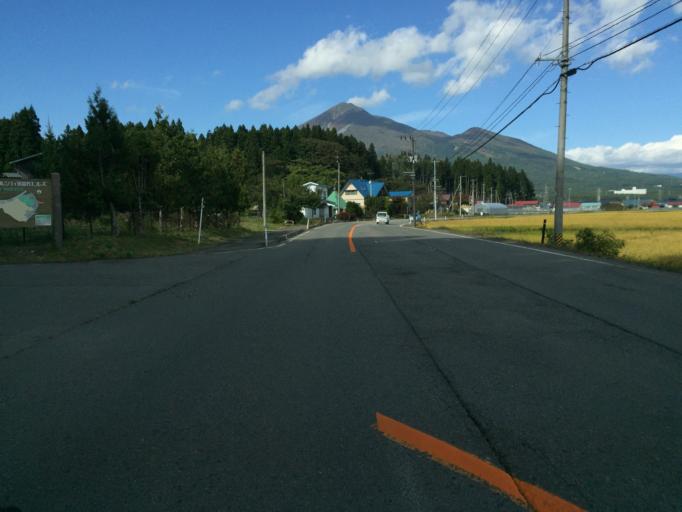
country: JP
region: Fukushima
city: Inawashiro
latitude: 37.5396
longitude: 140.0630
